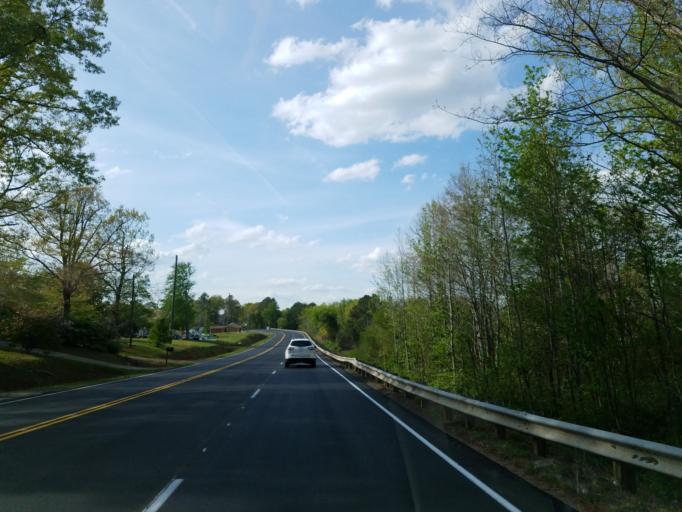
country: US
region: Georgia
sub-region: Pickens County
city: Jasper
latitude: 34.4494
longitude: -84.4037
